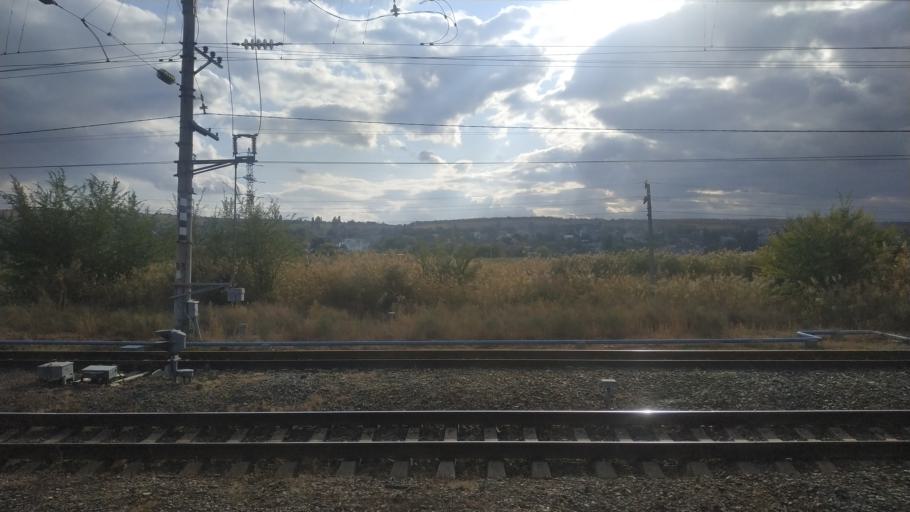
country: RU
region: Volgograd
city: Krasnoslobodsk
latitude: 48.5180
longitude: 44.5147
